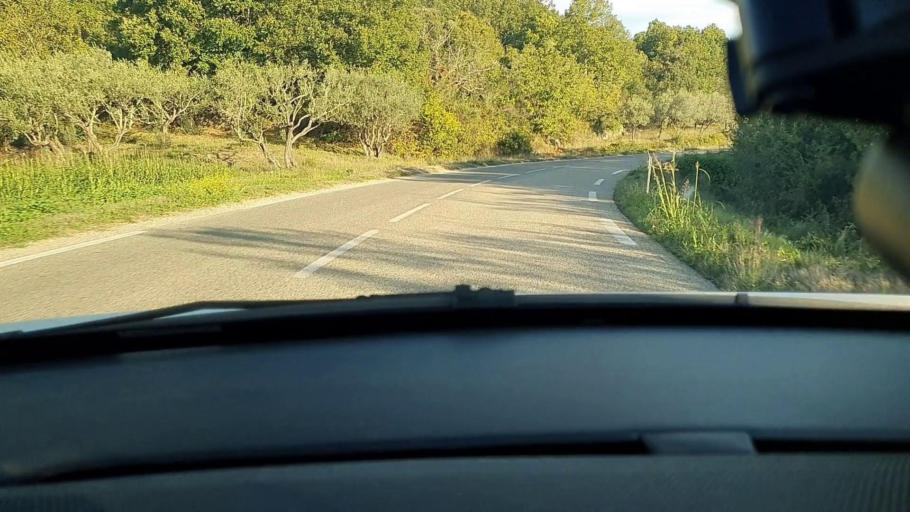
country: FR
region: Languedoc-Roussillon
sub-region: Departement du Gard
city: Barjac
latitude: 44.2357
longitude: 4.3042
